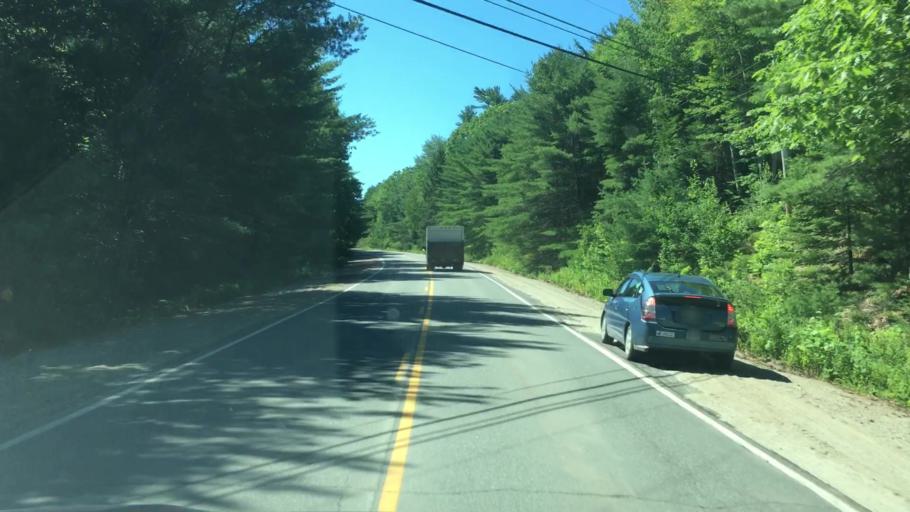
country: US
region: Maine
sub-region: Hancock County
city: Sedgwick
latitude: 44.3774
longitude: -68.5684
